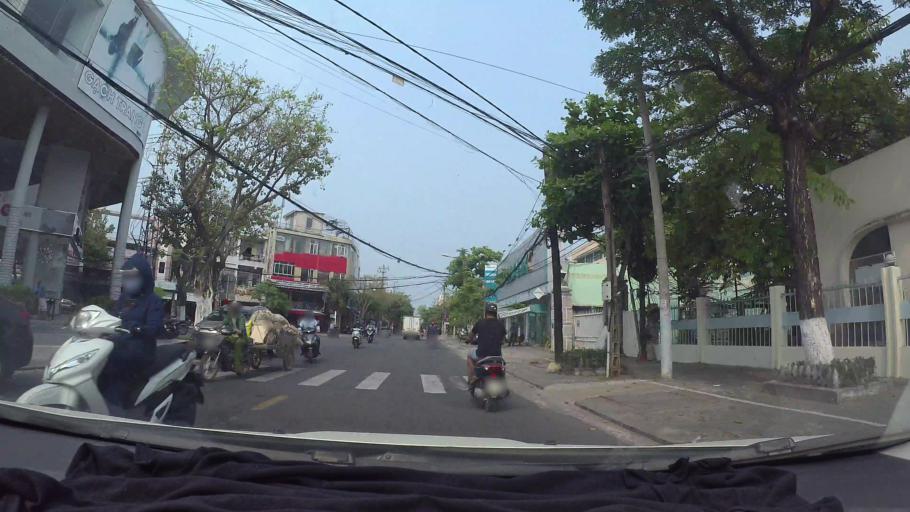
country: VN
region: Da Nang
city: Da Nang
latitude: 16.0496
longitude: 108.2144
